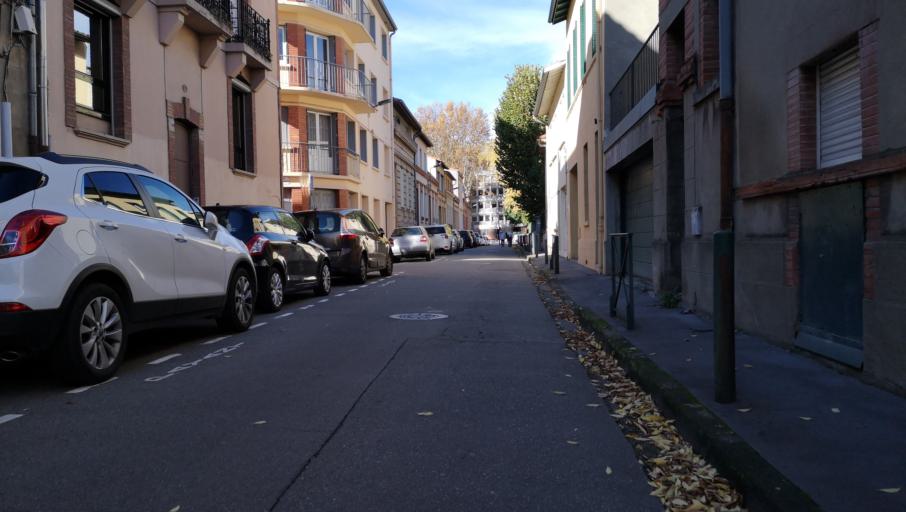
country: FR
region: Midi-Pyrenees
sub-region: Departement de la Haute-Garonne
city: Toulouse
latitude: 43.6078
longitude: 1.4310
